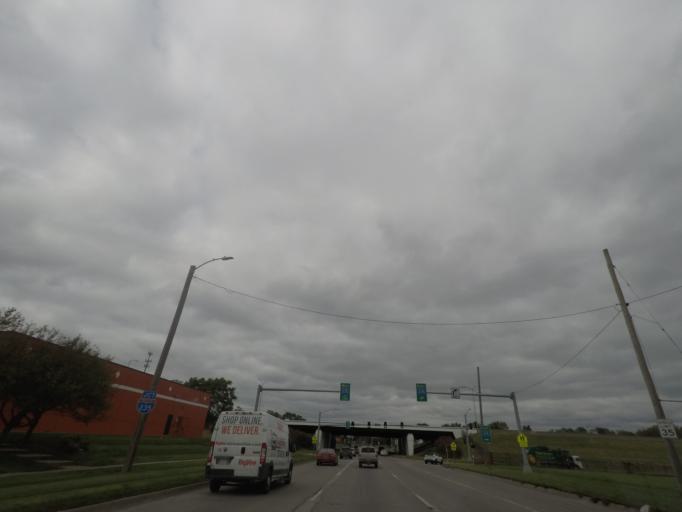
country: US
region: Iowa
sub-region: Polk County
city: Des Moines
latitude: 41.5954
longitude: -93.5959
